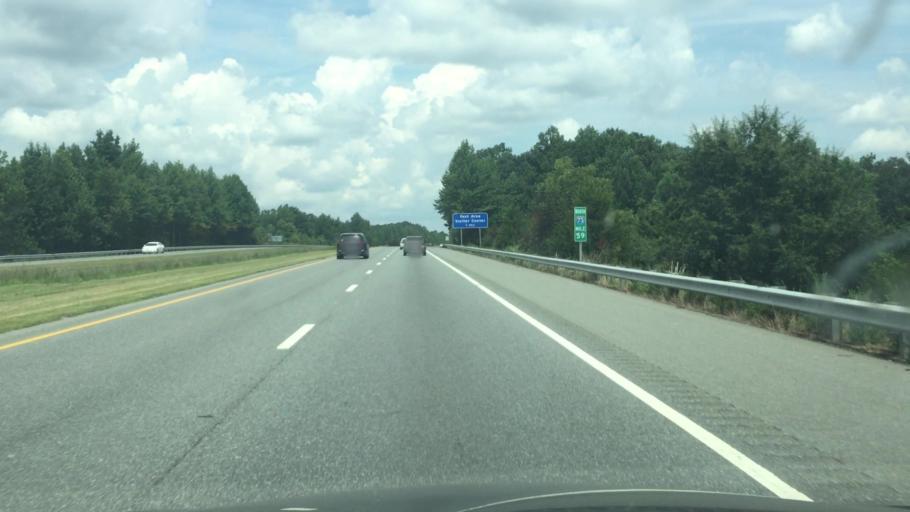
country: US
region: North Carolina
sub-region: Montgomery County
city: Biscoe
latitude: 35.4979
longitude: -79.7807
